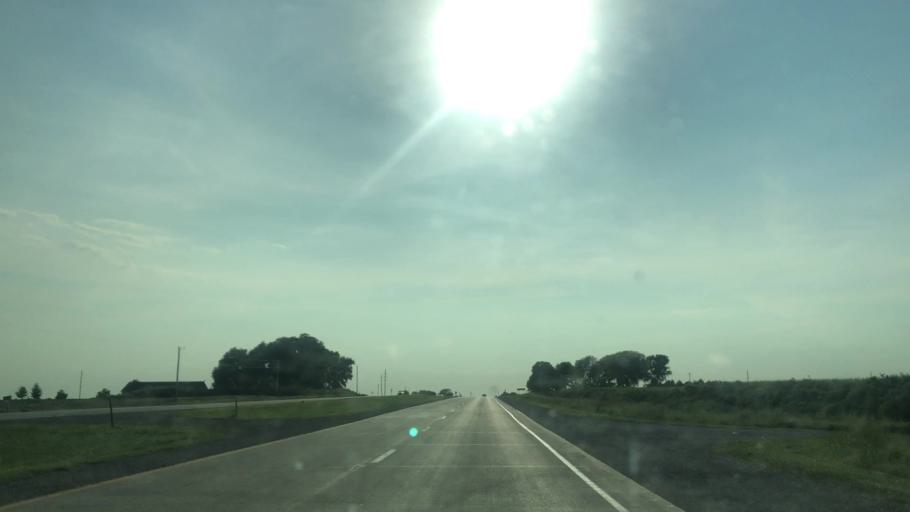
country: US
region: Iowa
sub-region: Story County
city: Nevada
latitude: 42.0079
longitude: -93.4003
